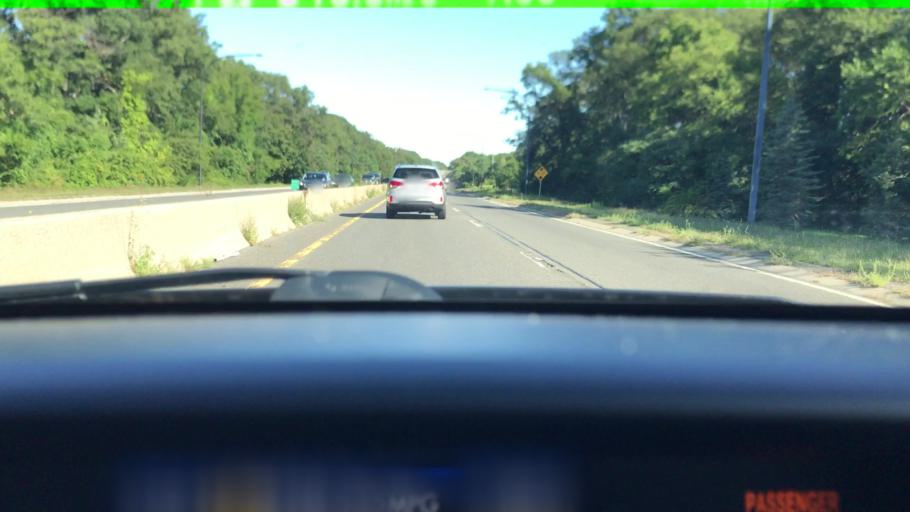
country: US
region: New York
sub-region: Nassau County
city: Salisbury
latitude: 40.7448
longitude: -73.5461
